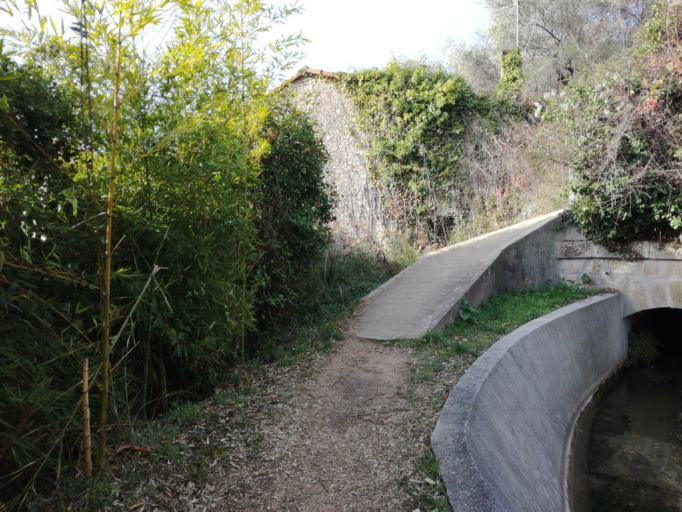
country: FR
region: Provence-Alpes-Cote d'Azur
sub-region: Departement des Alpes-Maritimes
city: Mouans-Sartoux
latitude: 43.6134
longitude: 6.9846
